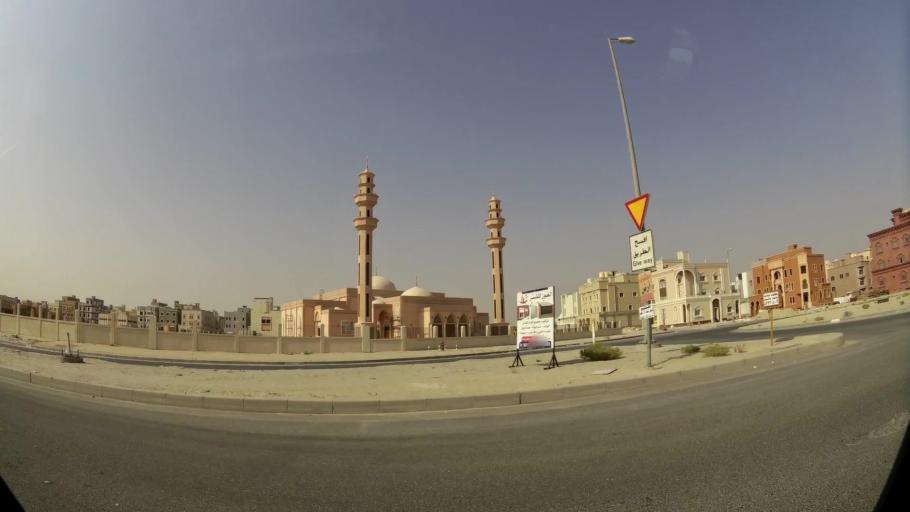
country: KW
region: Muhafazat al Jahra'
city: Al Jahra'
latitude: 29.3535
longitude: 47.7705
